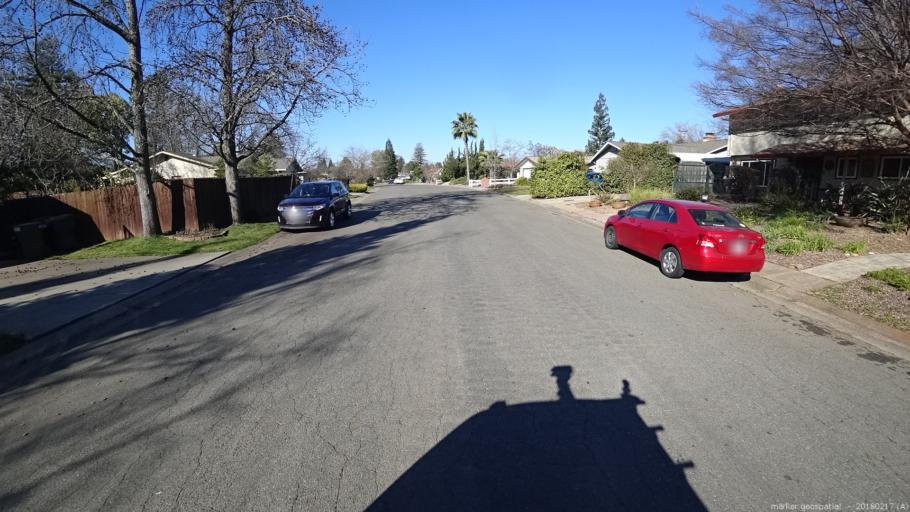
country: US
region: California
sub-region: Sacramento County
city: Folsom
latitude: 38.6650
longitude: -121.1995
